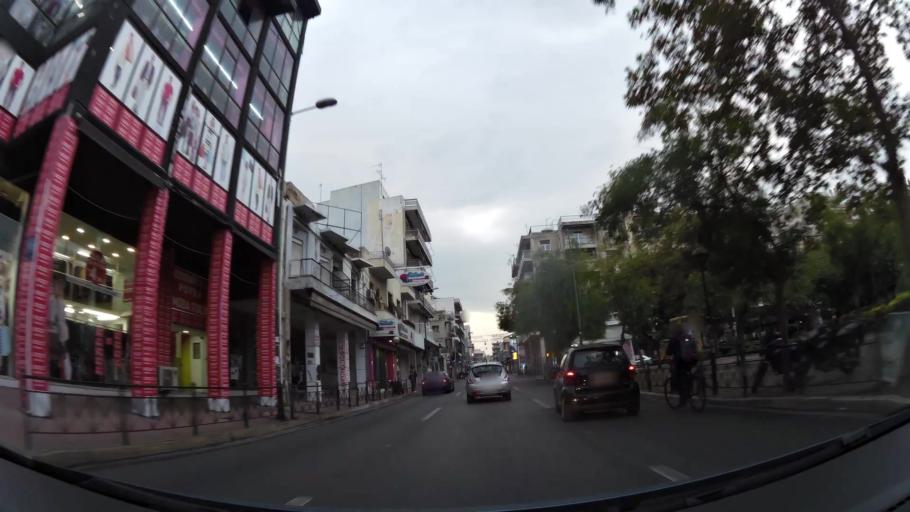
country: GR
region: Attica
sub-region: Nomarchia Athinas
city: Dhafni
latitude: 37.9566
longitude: 23.7355
